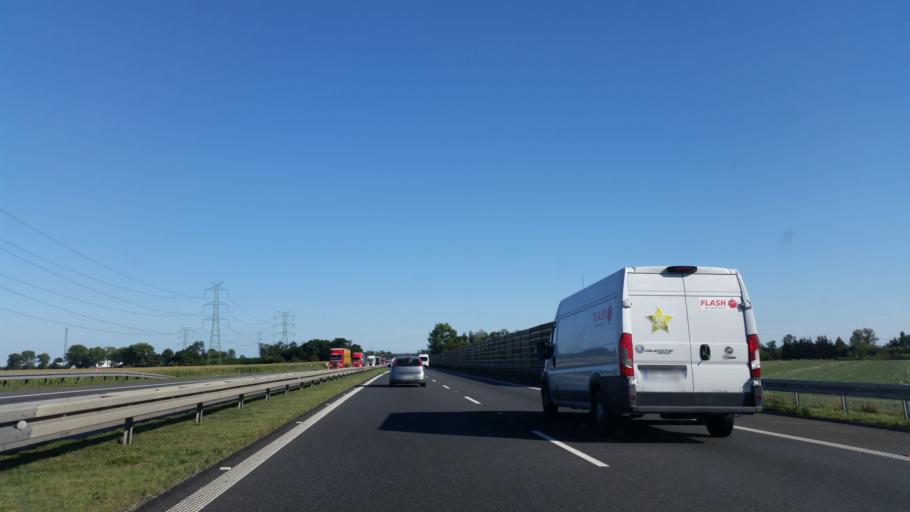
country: PL
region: Lower Silesian Voivodeship
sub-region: Powiat olawski
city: Wierzbno
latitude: 50.8930
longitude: 17.1839
